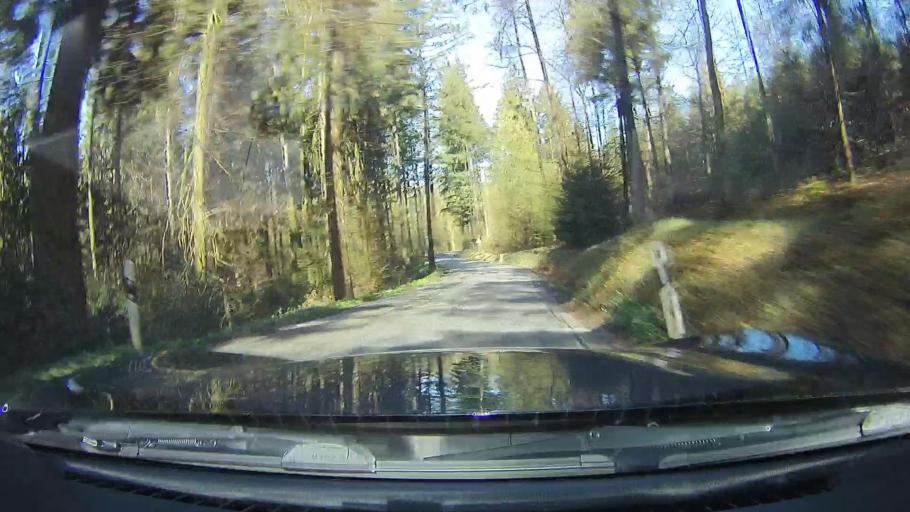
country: DE
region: Baden-Wuerttemberg
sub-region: Karlsruhe Region
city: Eberbach
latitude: 49.4184
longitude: 8.9644
